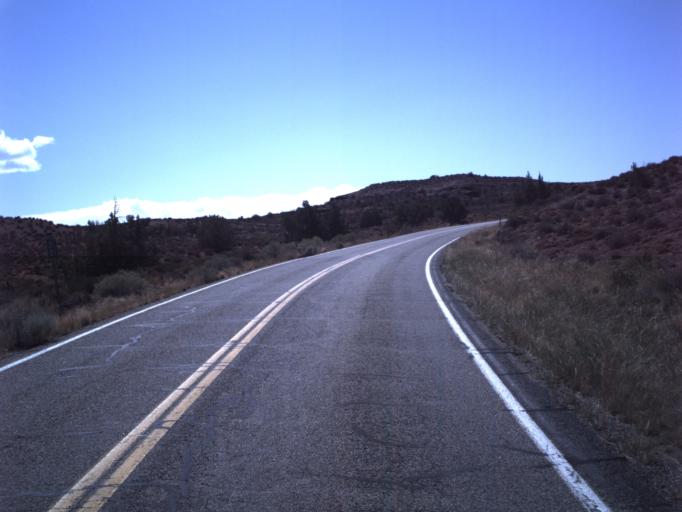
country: US
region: Utah
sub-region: Grand County
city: Moab
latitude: 38.7421
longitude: -109.3315
